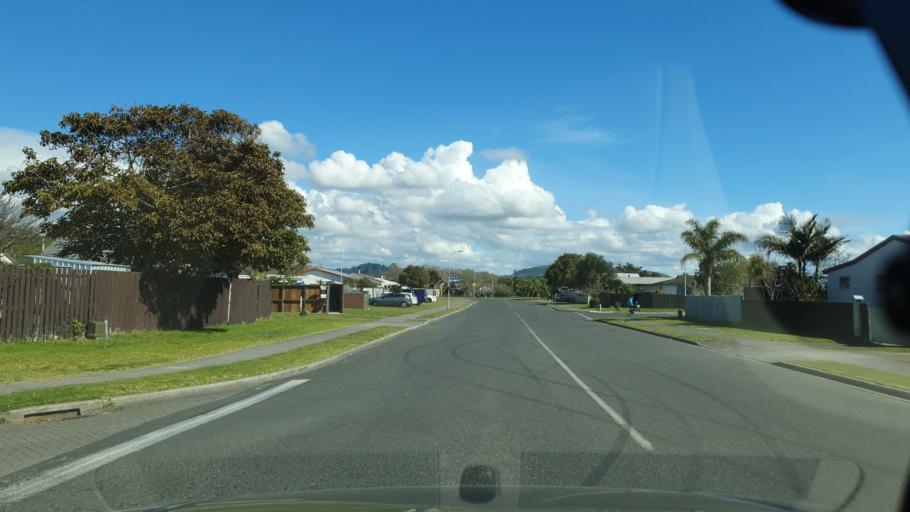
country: NZ
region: Bay of Plenty
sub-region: Tauranga City
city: Tauranga
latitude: -37.7032
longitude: 176.2933
